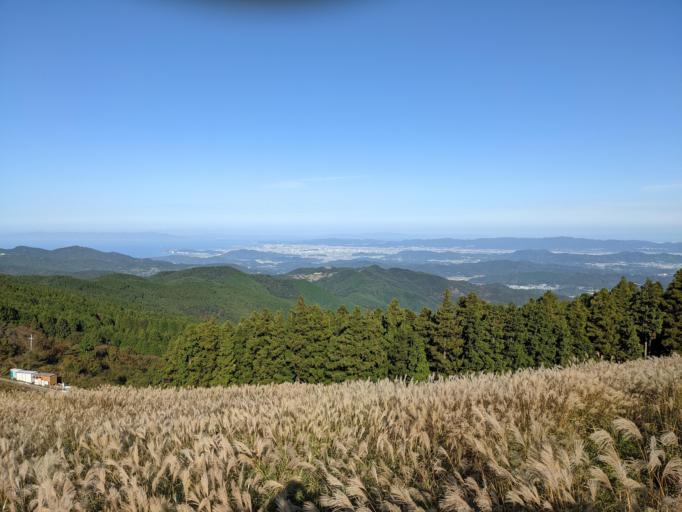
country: JP
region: Wakayama
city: Kainan
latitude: 34.1055
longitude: 135.3284
